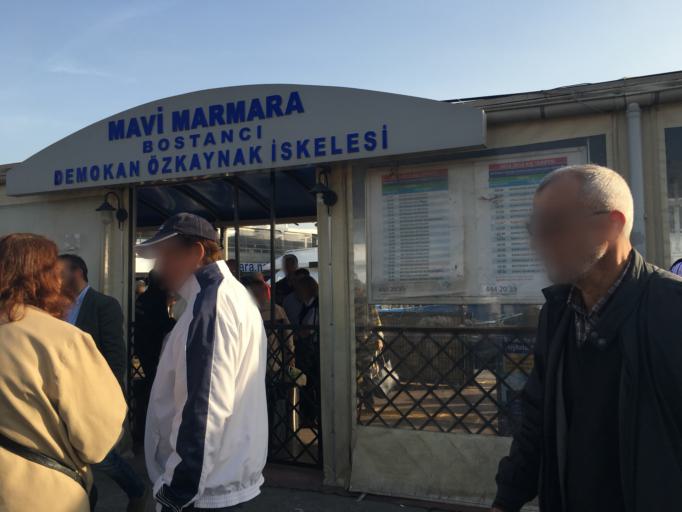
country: TR
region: Istanbul
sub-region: Atasehir
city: Atasehir
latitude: 40.9524
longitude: 29.0940
